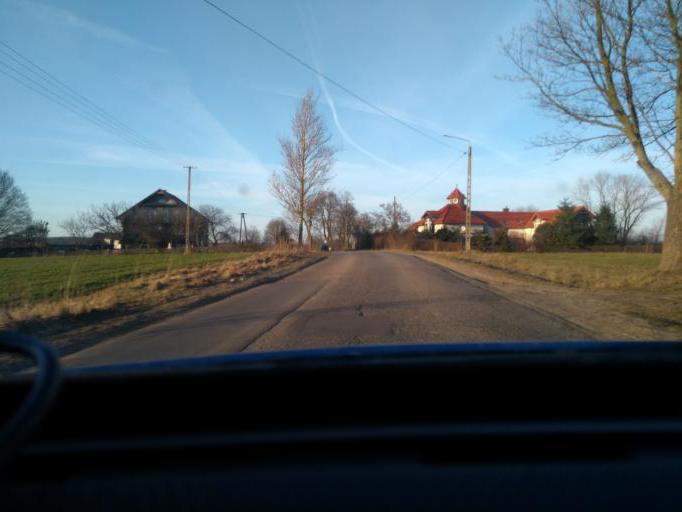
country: PL
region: Pomeranian Voivodeship
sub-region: Powiat kartuski
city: Przodkowo
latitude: 54.3962
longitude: 18.2890
